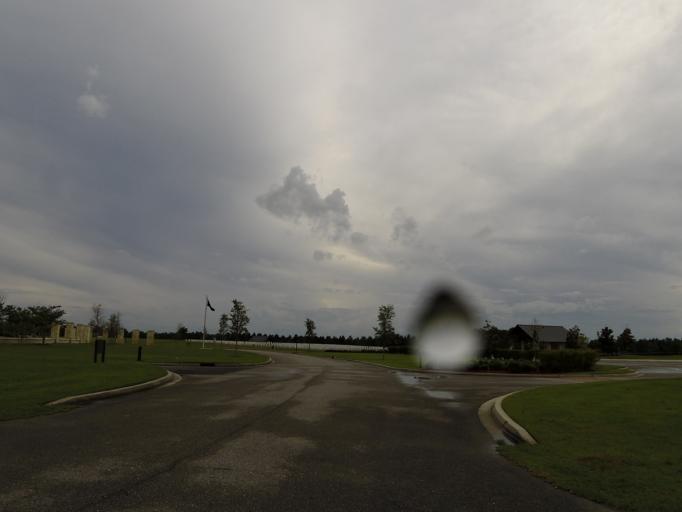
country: US
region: Florida
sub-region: Nassau County
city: Nassau Village-Ratliff
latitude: 30.5487
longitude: -81.7204
